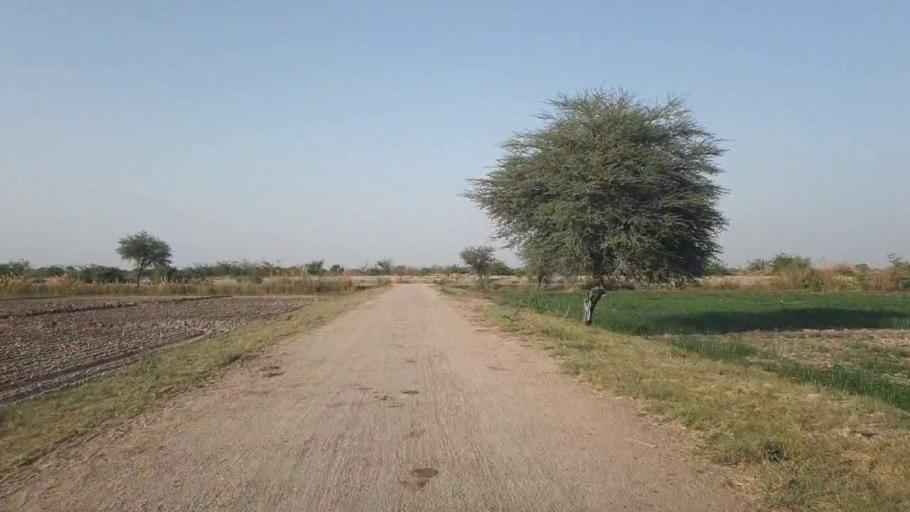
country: PK
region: Sindh
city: Dhoro Naro
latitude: 25.4843
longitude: 69.5811
